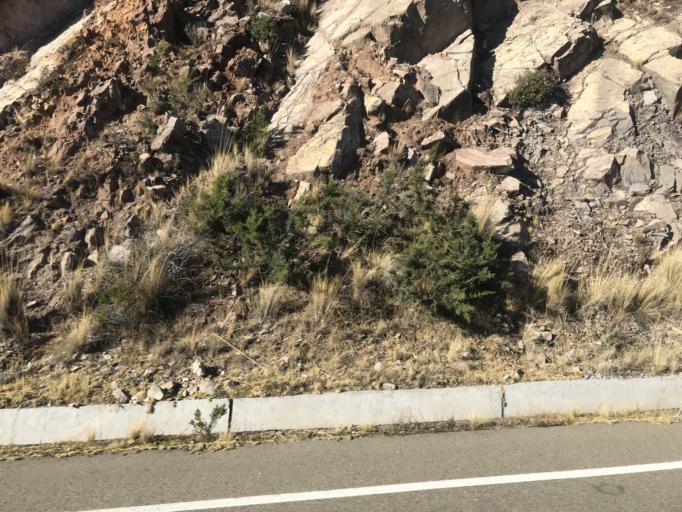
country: BO
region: La Paz
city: San Pedro
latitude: -16.1891
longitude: -68.9271
